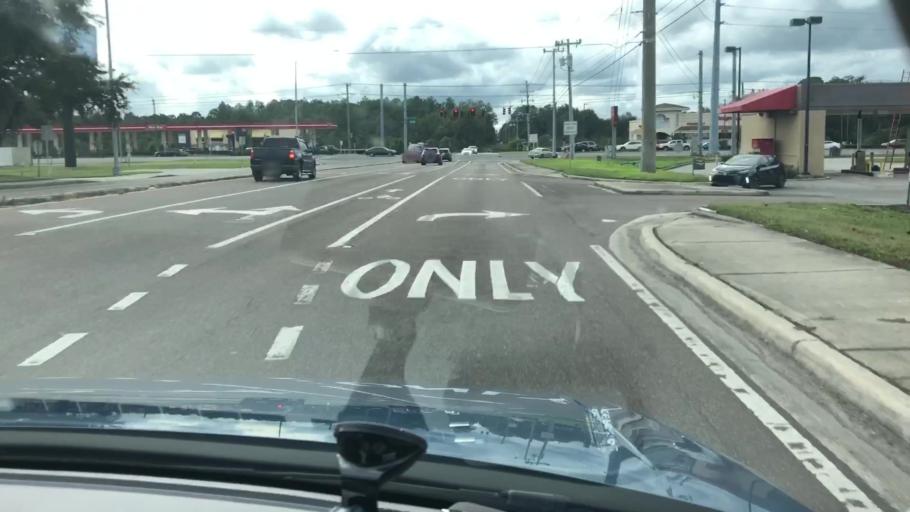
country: US
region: Florida
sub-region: Polk County
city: Gibsonia
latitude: 28.1282
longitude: -81.9723
